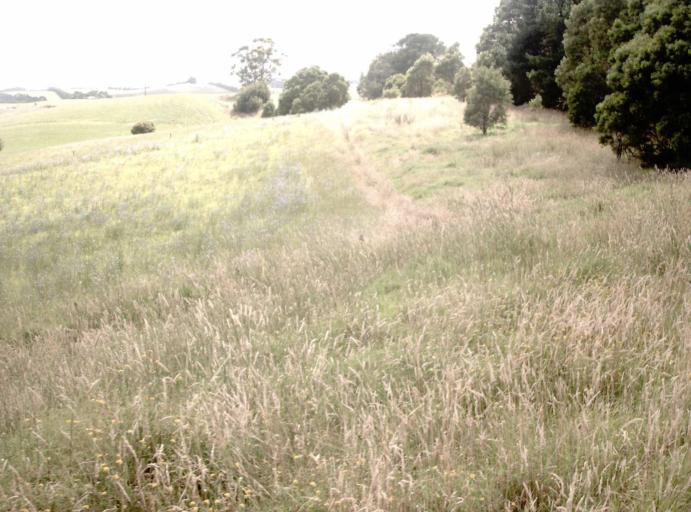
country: AU
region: Victoria
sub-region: Cardinia
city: Bunyip
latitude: -38.3444
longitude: 145.7478
